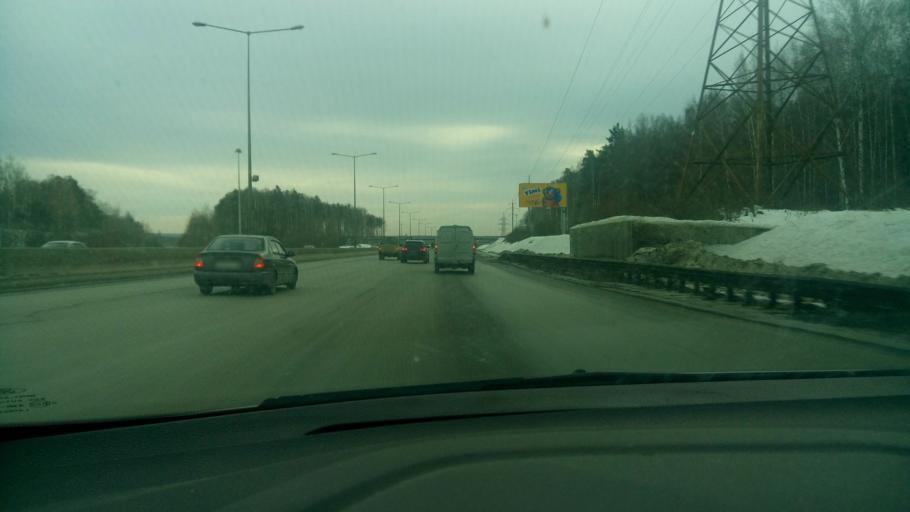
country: RU
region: Sverdlovsk
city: Istok
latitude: 56.7714
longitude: 60.7264
